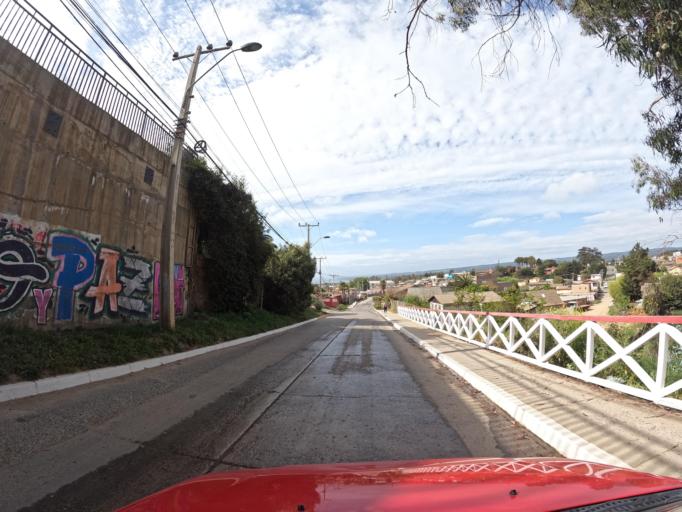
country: CL
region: O'Higgins
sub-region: Provincia de Colchagua
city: Santa Cruz
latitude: -34.3893
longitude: -72.0009
